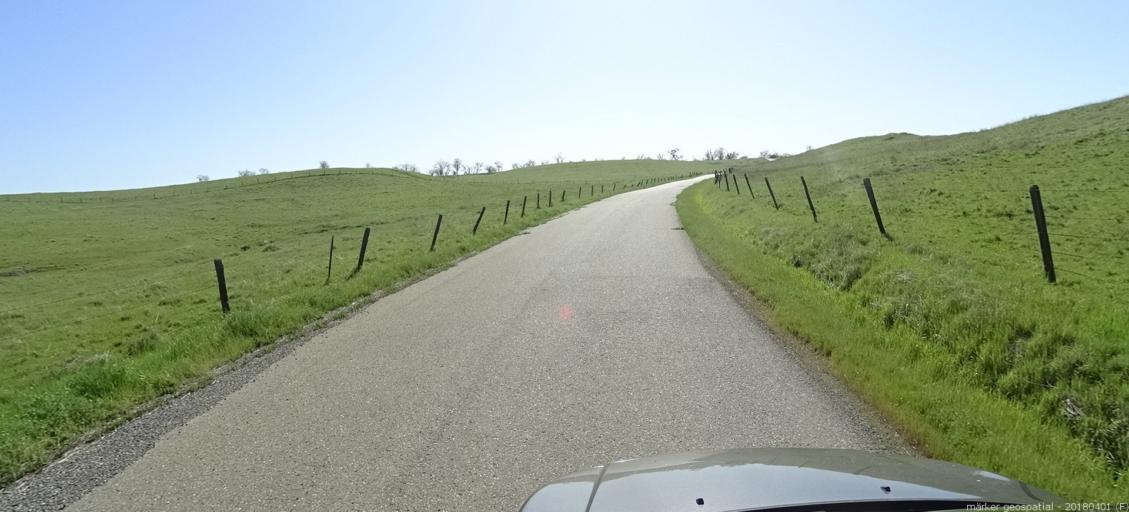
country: US
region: California
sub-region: Sacramento County
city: Rancho Murieta
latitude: 38.4642
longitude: -121.1154
